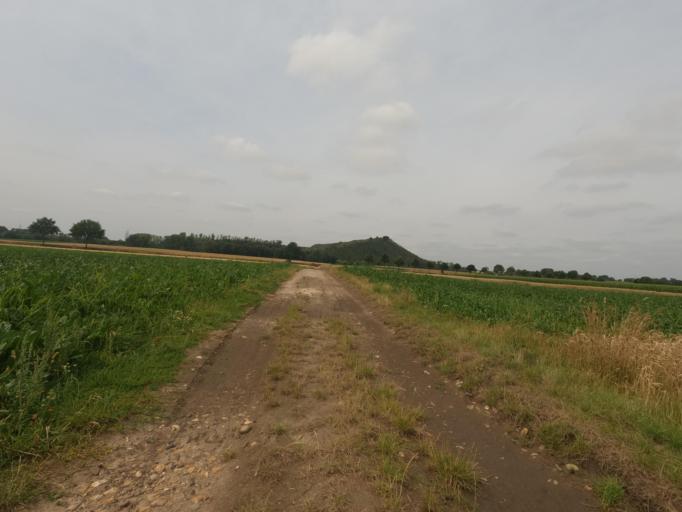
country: DE
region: North Rhine-Westphalia
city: Siersdorf
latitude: 50.9152
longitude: 6.2430
